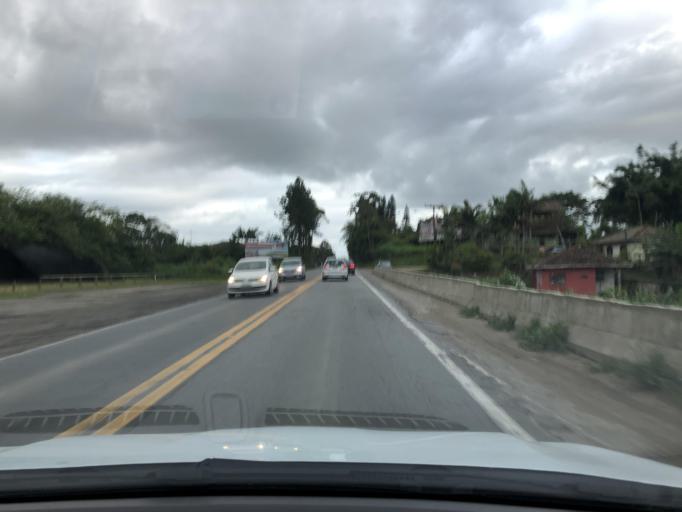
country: BR
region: Santa Catarina
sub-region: Sao Francisco Do Sul
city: Sao Francisco do Sul
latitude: -26.2844
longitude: -48.6463
